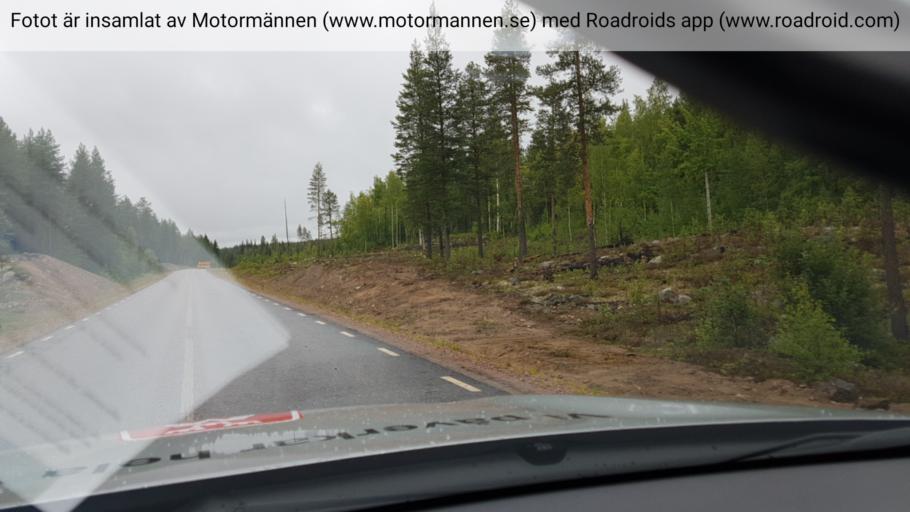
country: SE
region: Norrbotten
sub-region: Gallivare Kommun
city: Gaellivare
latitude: 66.6804
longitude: 20.3657
